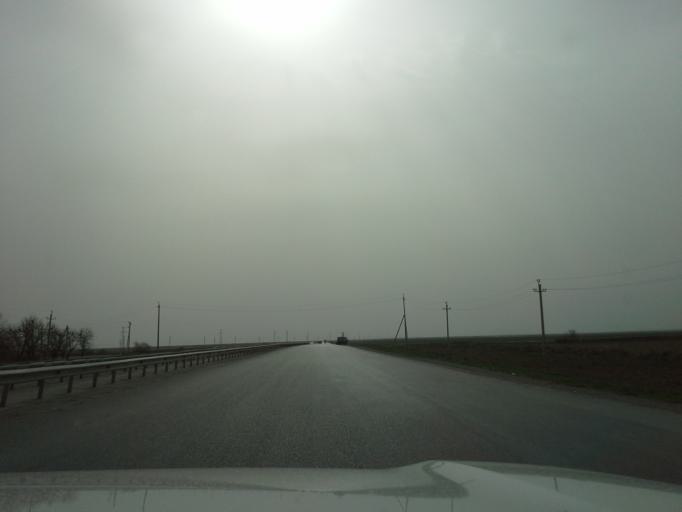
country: IR
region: Razavi Khorasan
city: Dargaz
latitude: 37.5537
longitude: 59.3747
